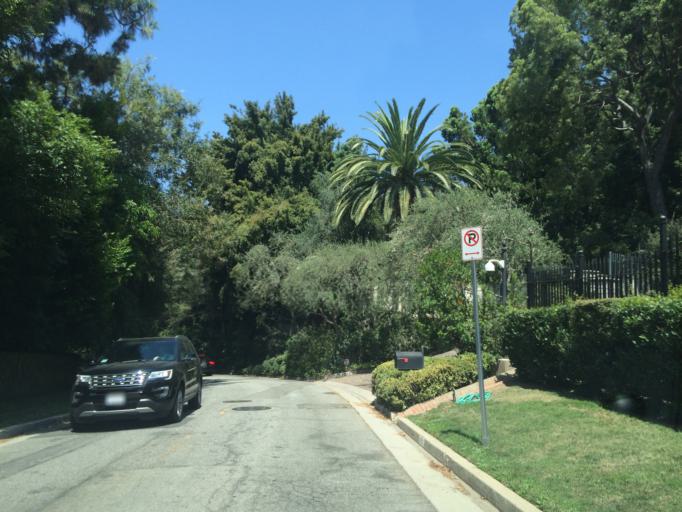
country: US
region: California
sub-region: Los Angeles County
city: Westwood, Los Angeles
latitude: 34.0826
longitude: -118.4419
